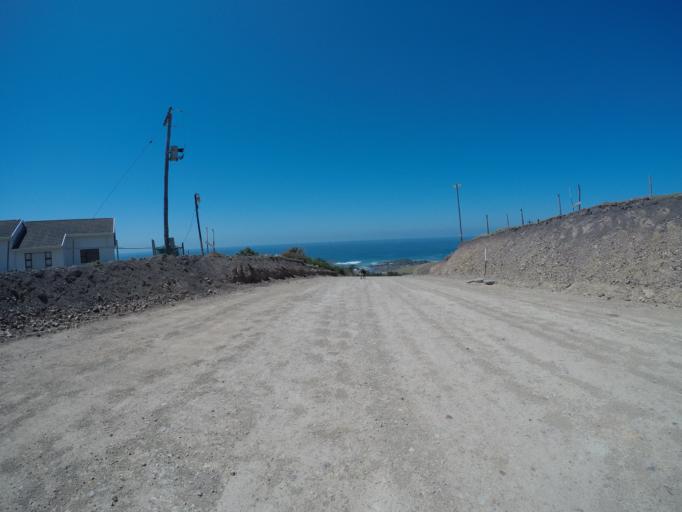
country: ZA
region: Eastern Cape
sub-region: OR Tambo District Municipality
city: Libode
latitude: -32.0342
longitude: 29.1095
